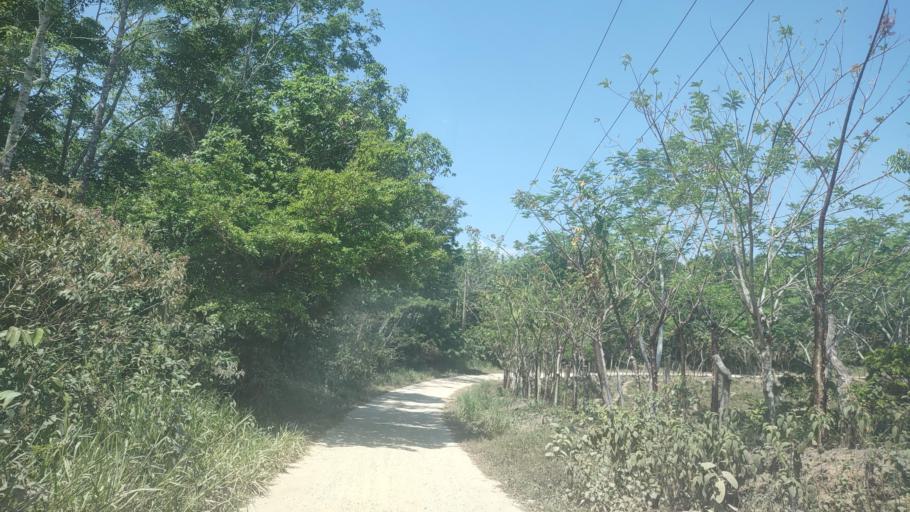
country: MX
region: Veracruz
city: Las Choapas
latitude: 17.7885
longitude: -94.1513
